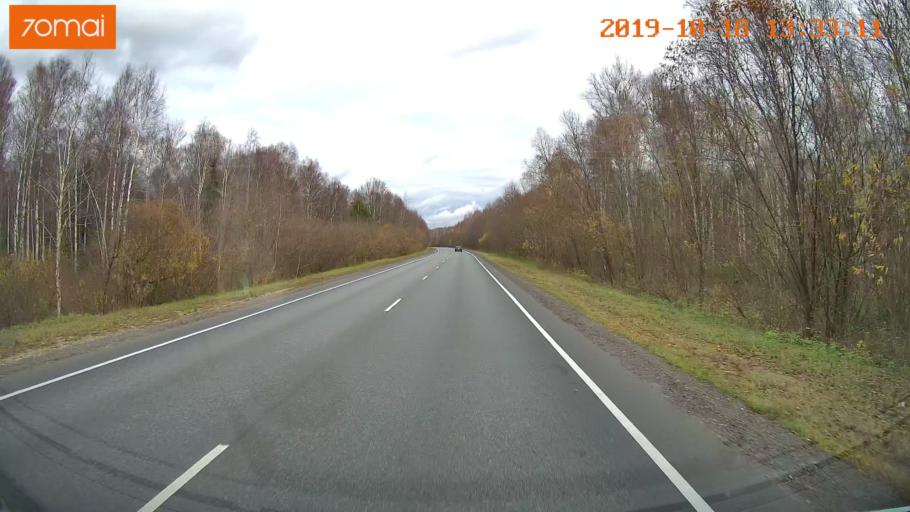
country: RU
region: Rjazan
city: Solotcha
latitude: 54.8404
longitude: 39.9310
